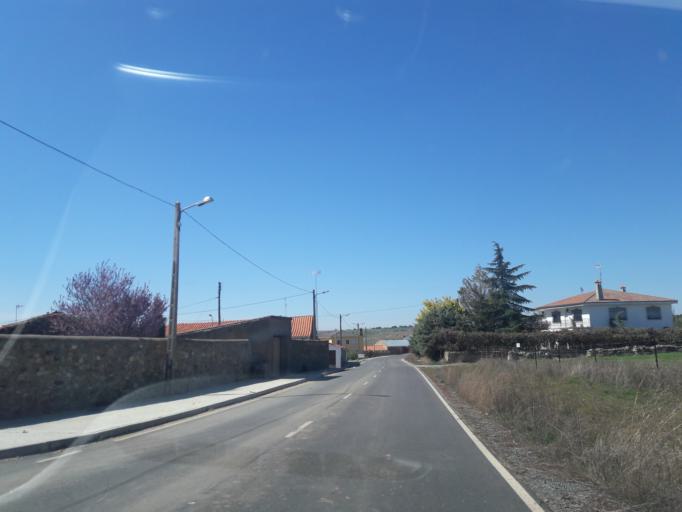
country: ES
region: Castille and Leon
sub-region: Provincia de Salamanca
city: Martinamor
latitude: 40.8075
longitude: -5.5988
